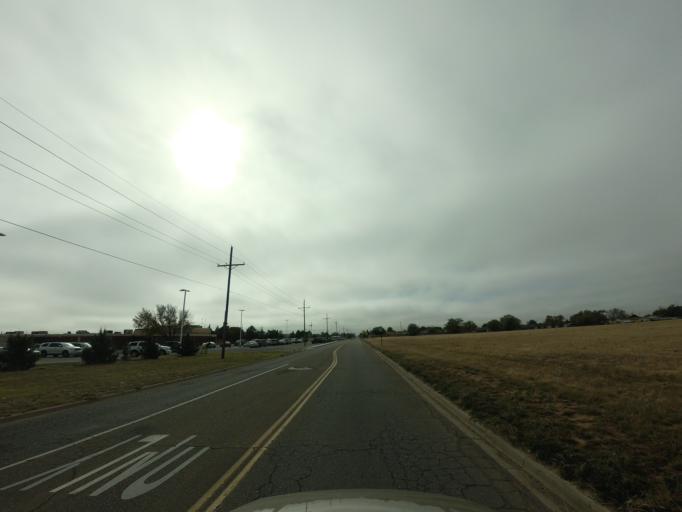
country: US
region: New Mexico
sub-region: Curry County
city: Clovis
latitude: 34.4337
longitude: -103.2140
